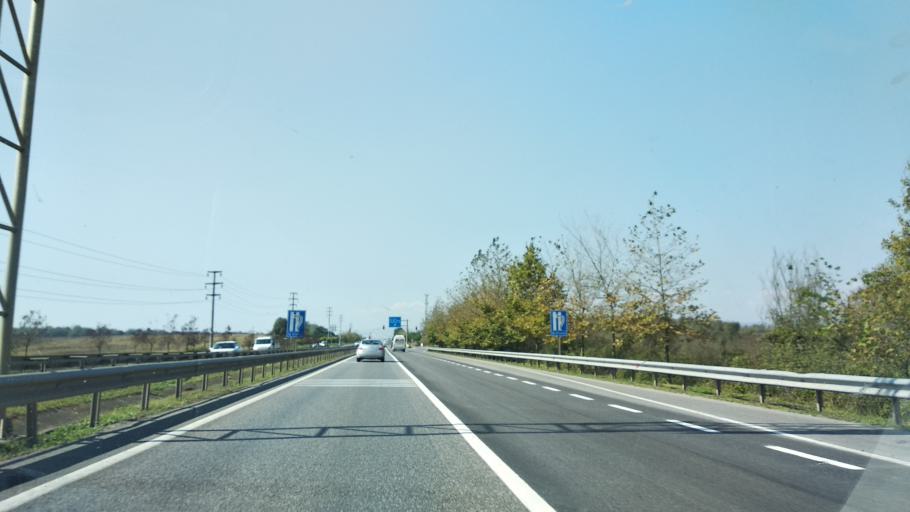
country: TR
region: Kocaeli
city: Derbent
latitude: 40.7429
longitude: 30.0839
